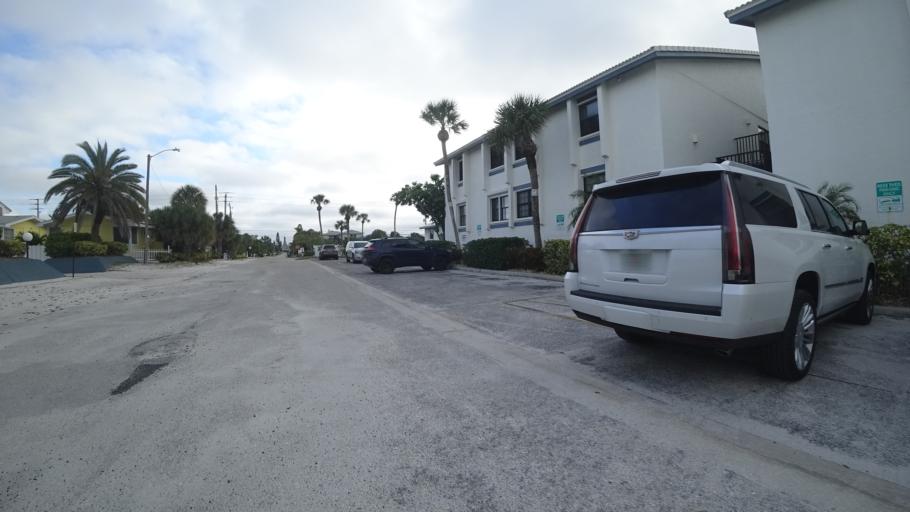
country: US
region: Florida
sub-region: Manatee County
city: Anna Maria
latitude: 27.5128
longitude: -82.7232
